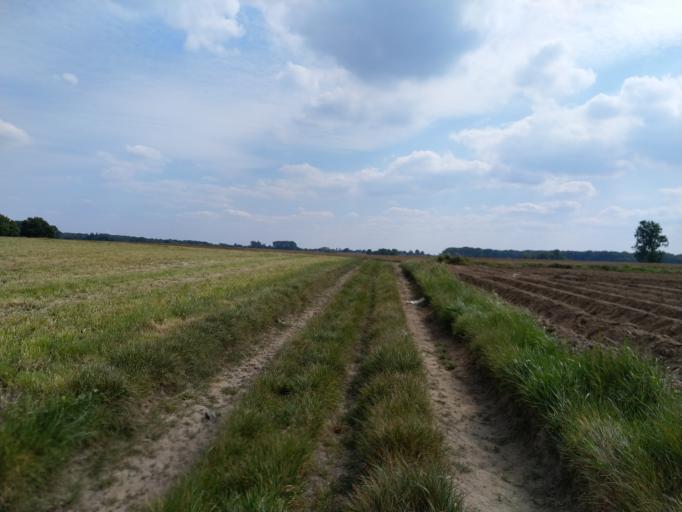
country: BE
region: Wallonia
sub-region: Province du Hainaut
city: Jurbise
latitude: 50.5291
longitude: 3.9555
